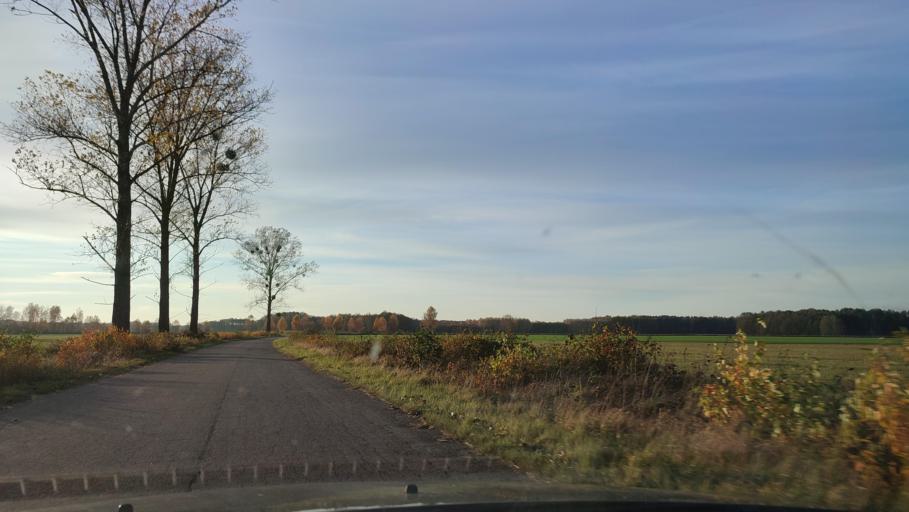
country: PL
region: Masovian Voivodeship
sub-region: Powiat mlawski
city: Dzierzgowo
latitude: 53.3324
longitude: 20.7155
